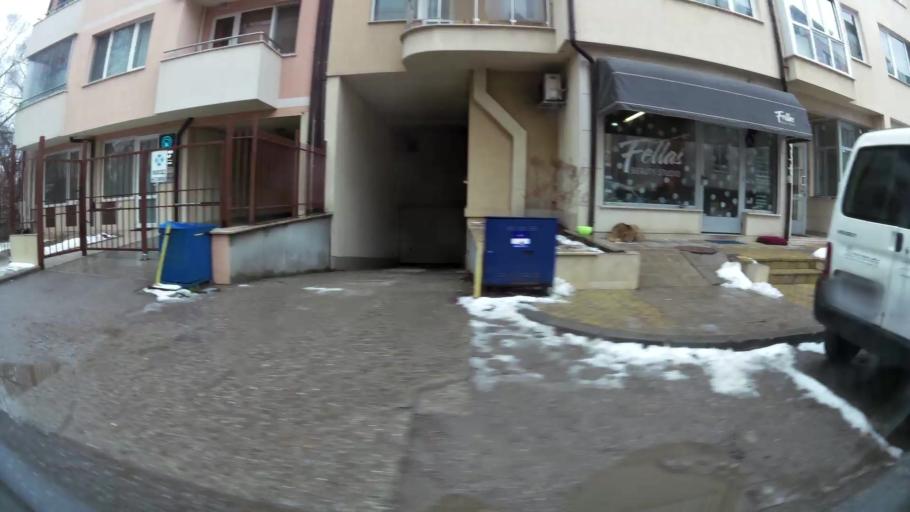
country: BG
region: Sofia-Capital
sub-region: Stolichna Obshtina
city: Sofia
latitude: 42.6581
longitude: 23.2987
